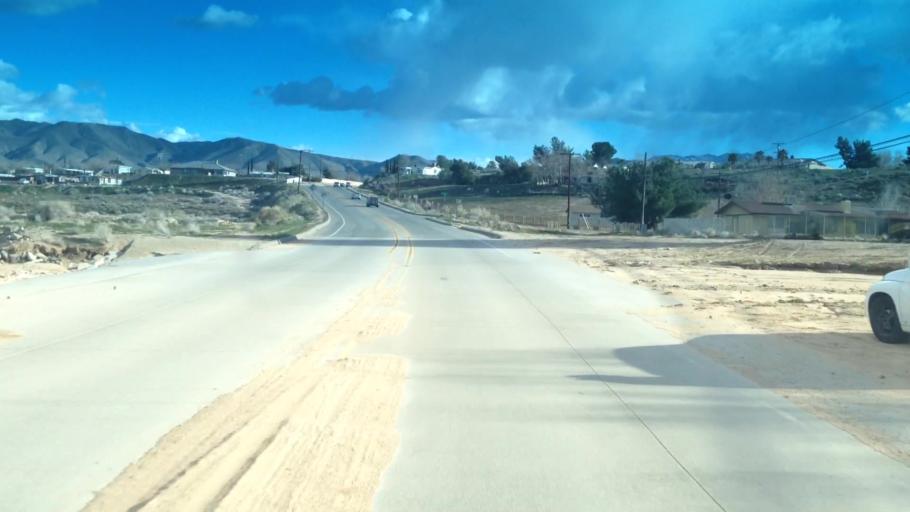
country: US
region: California
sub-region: San Bernardino County
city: Hesperia
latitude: 34.4078
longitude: -117.2522
